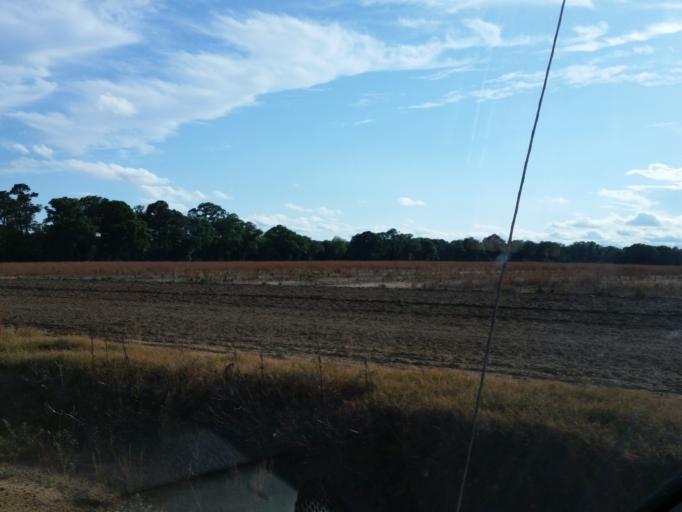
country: US
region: Georgia
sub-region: Dooly County
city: Vienna
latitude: 32.0318
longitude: -83.7732
